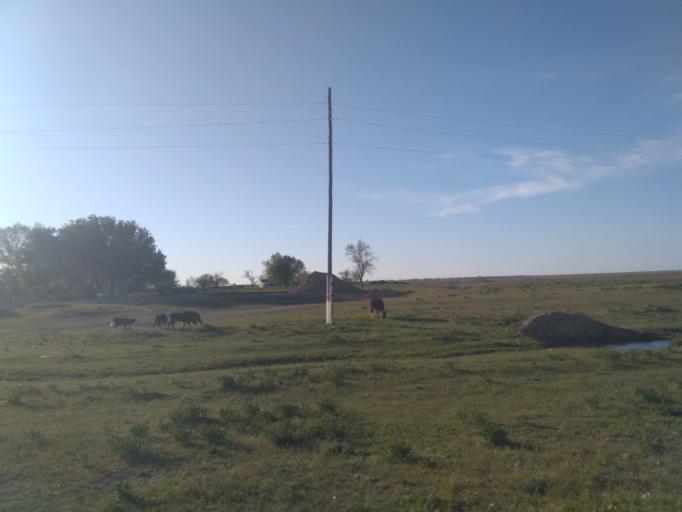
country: KZ
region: Ongtustik Qazaqstan
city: Ashchysay
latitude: 43.6935
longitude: 68.9946
